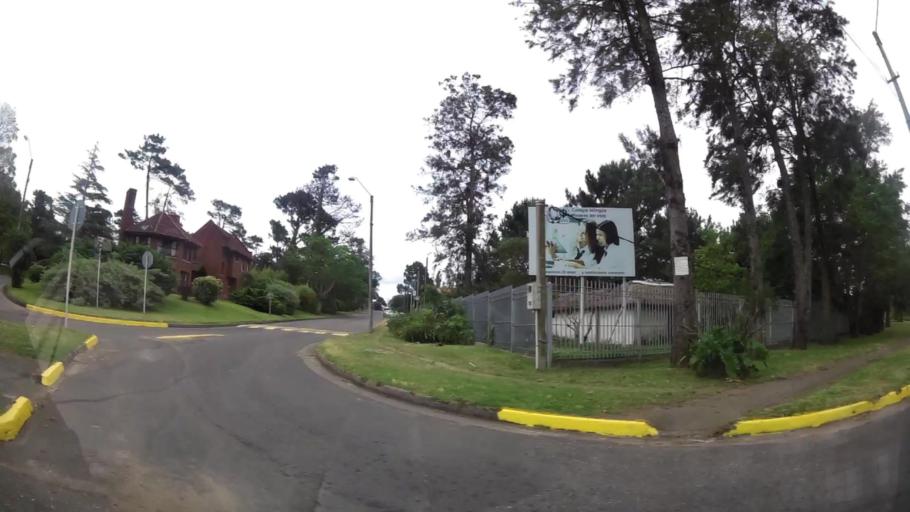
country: UY
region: Maldonado
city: Maldonado
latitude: -34.9119
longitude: -54.9726
